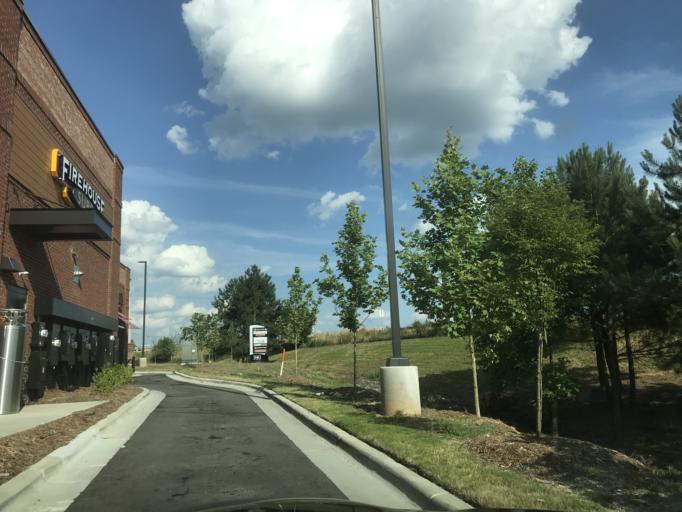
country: US
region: North Carolina
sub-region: Wake County
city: Wake Forest
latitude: 35.9692
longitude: -78.5470
